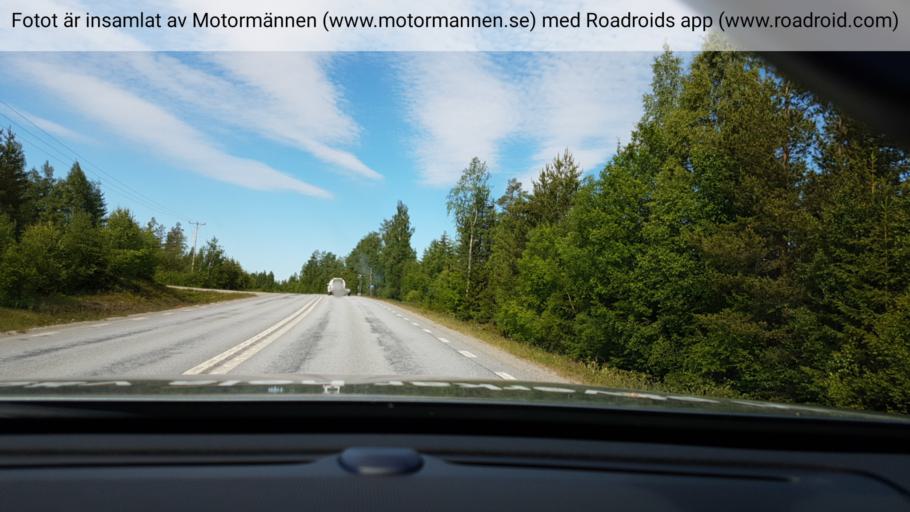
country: SE
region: Vaesterbotten
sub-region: Bjurholms Kommun
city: Bjurholm
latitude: 63.9351
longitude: 19.3217
